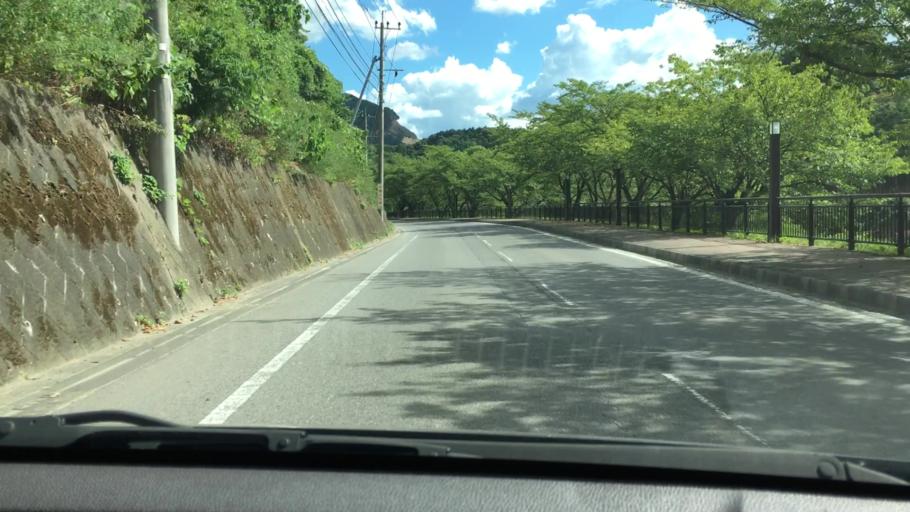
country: JP
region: Saga Prefecture
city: Takeocho-takeo
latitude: 33.1806
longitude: 130.0380
